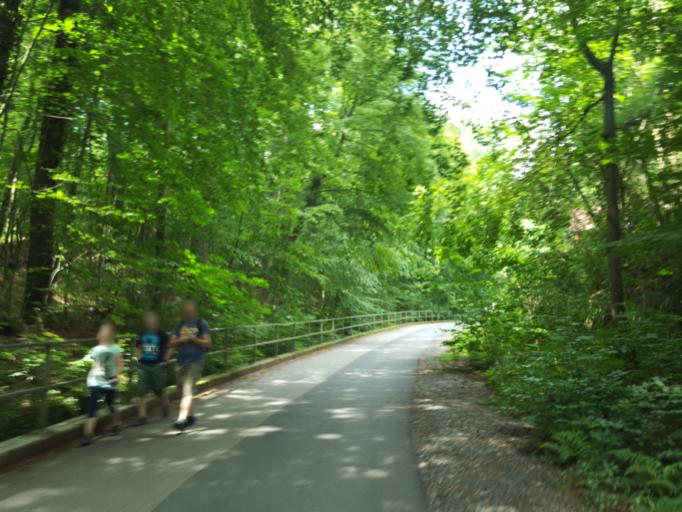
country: DE
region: Saxony
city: Albertstadt
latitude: 51.1134
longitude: 13.7874
